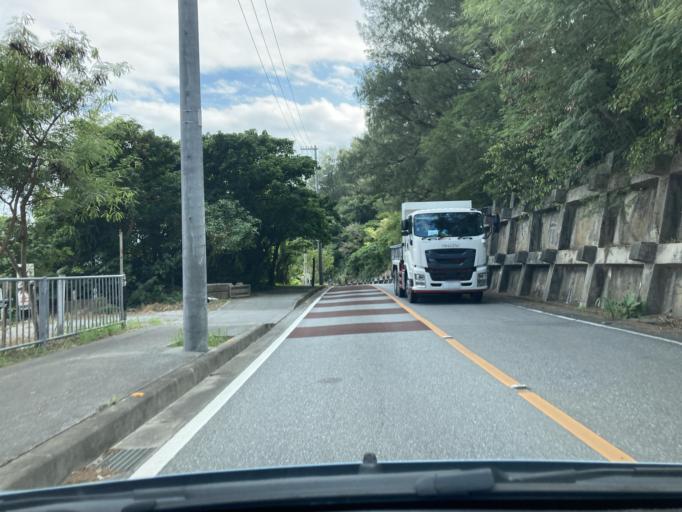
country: JP
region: Okinawa
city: Ginowan
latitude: 26.2623
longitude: 127.7836
